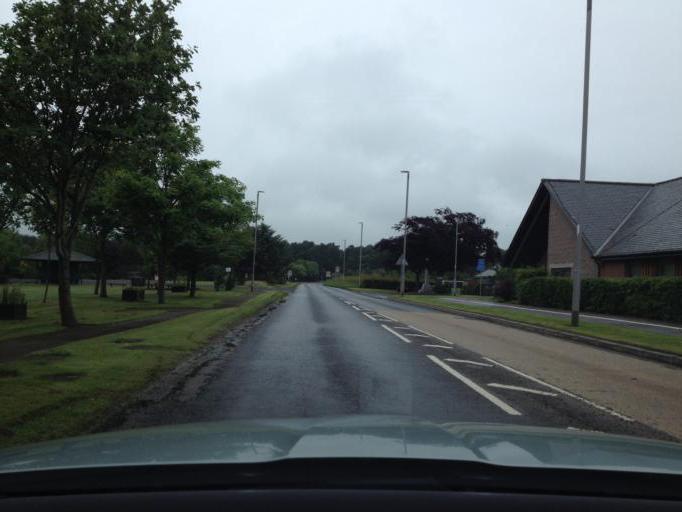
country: GB
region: Scotland
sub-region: Angus
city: Brechin
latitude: 56.8123
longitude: -2.6572
